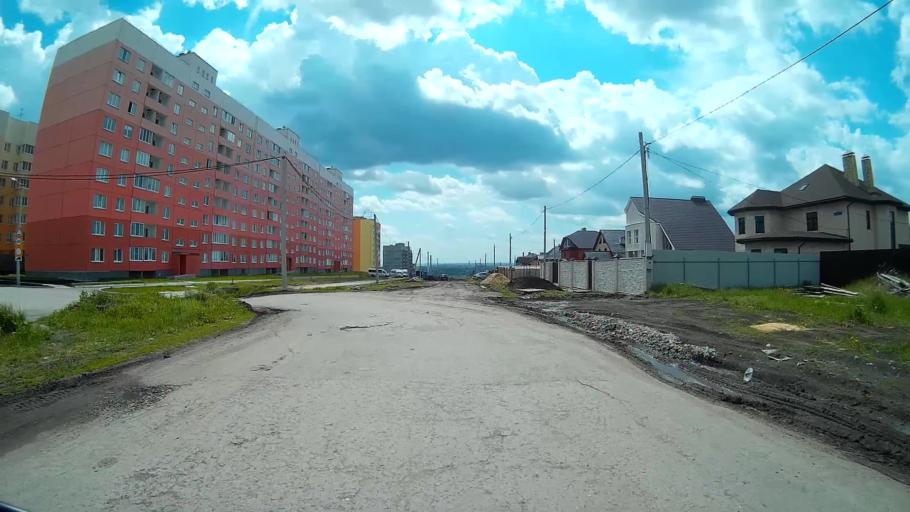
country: RU
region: Ulyanovsk
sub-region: Ulyanovskiy Rayon
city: Ulyanovsk
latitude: 54.3484
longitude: 48.3357
